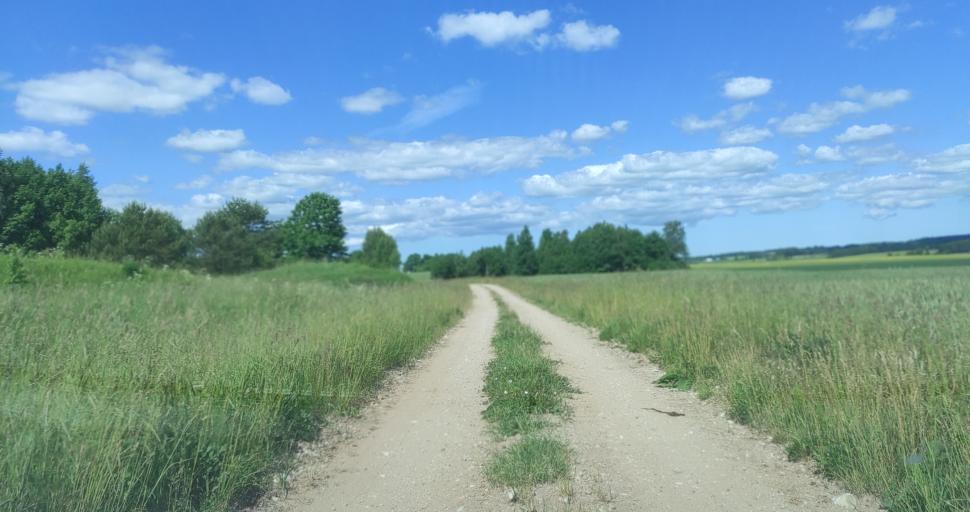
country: LV
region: Aizpute
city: Aizpute
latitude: 56.8555
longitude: 21.7170
